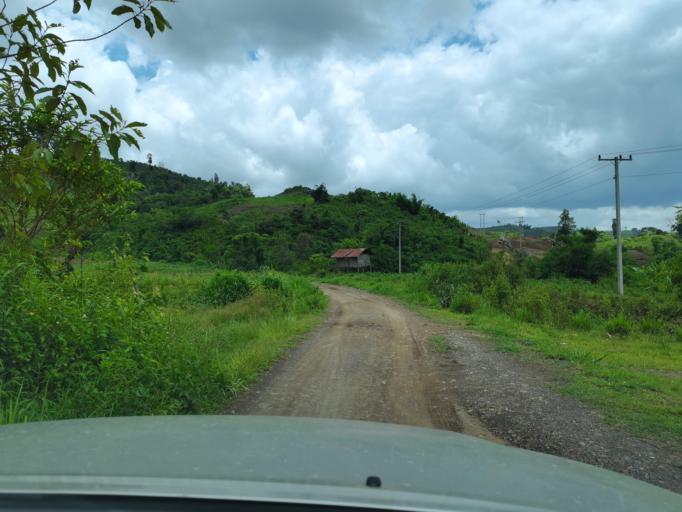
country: LA
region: Loungnamtha
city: Muang Long
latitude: 20.7340
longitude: 101.0141
